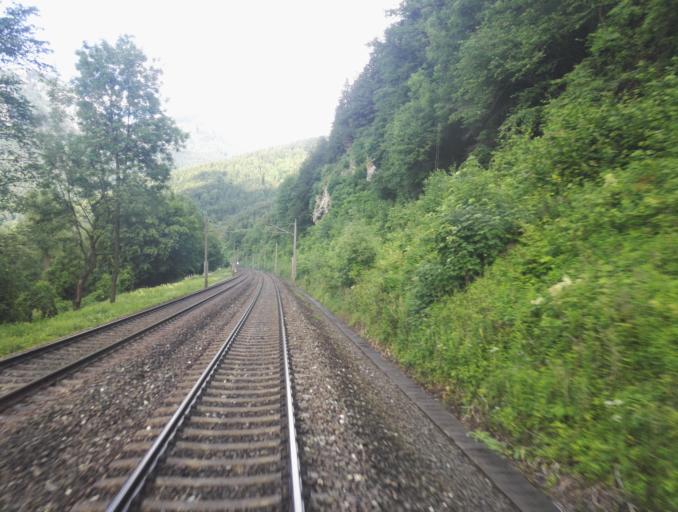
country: AT
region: Styria
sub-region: Politischer Bezirk Graz-Umgebung
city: Rothelstein
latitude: 47.3037
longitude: 15.3734
